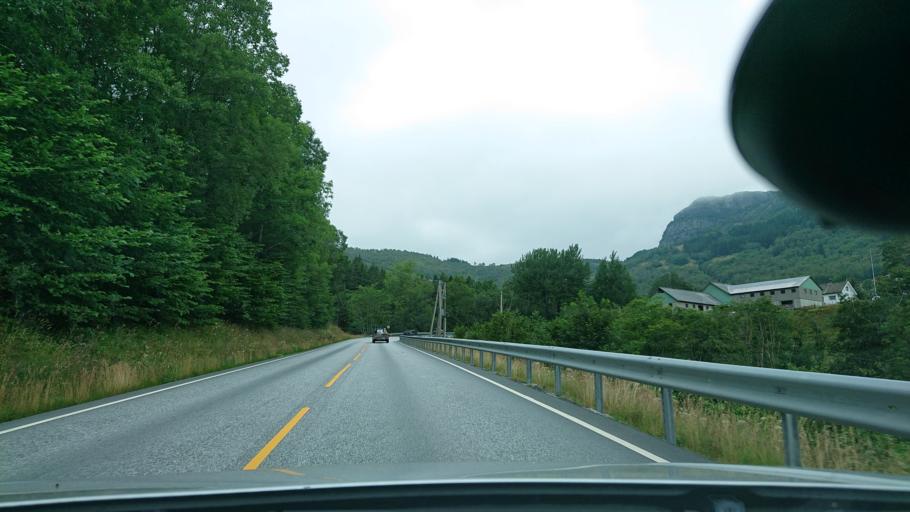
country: NO
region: Rogaland
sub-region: Hjelmeland
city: Hjelmelandsvagen
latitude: 59.1656
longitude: 6.1691
